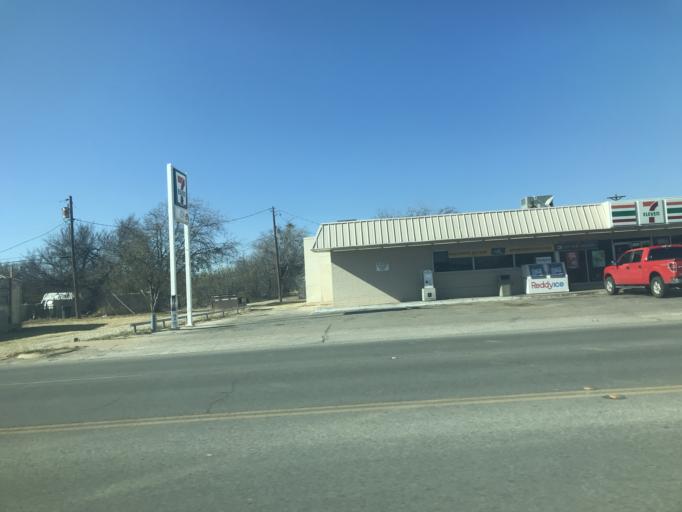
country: US
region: Texas
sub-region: Taylor County
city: Abilene
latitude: 32.4629
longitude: -99.7257
